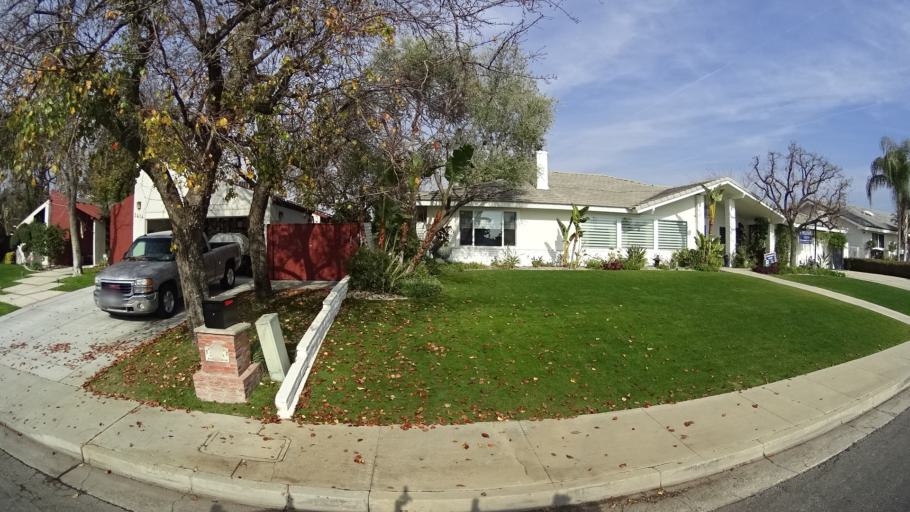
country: US
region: California
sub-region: Kern County
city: Oildale
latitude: 35.4137
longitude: -118.9656
